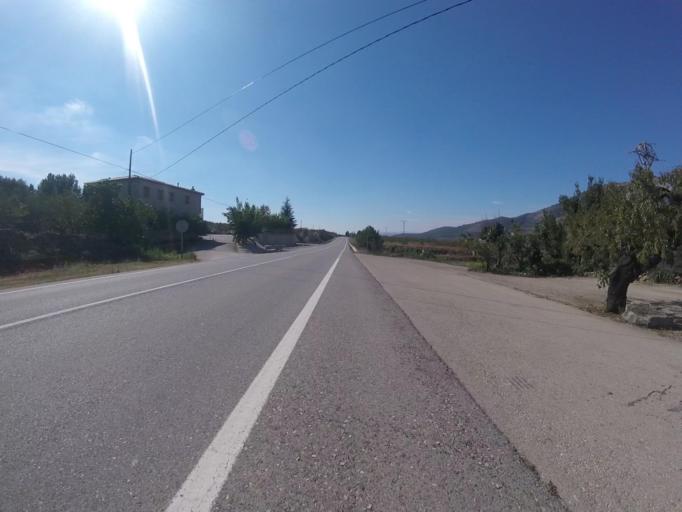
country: ES
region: Valencia
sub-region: Provincia de Castello
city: Sierra-Engarceran
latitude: 40.3022
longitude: -0.0440
